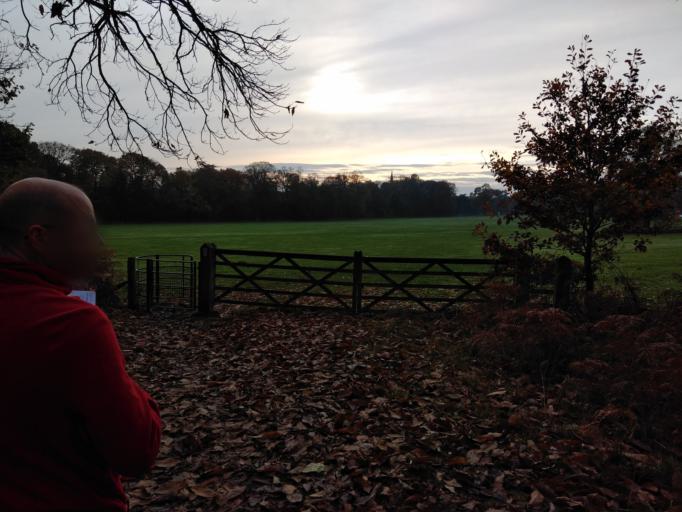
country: GB
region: England
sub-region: Nottinghamshire
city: Worksop
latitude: 53.2693
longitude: -1.0563
